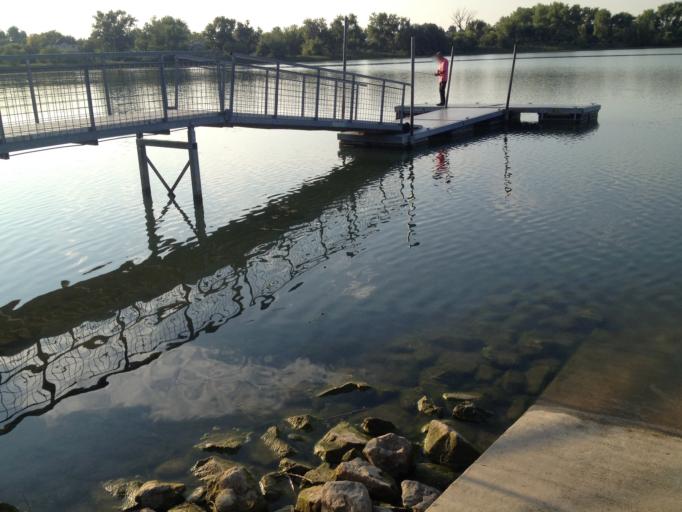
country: US
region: Colorado
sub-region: Boulder County
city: Lafayette
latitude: 39.9933
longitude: -105.1133
